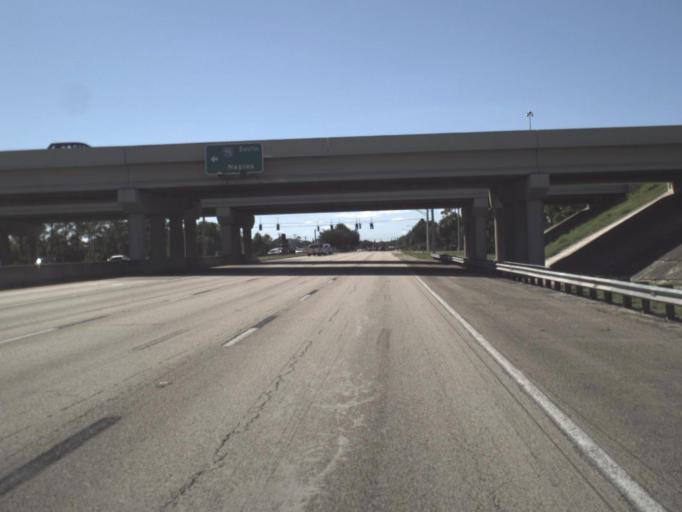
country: US
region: Florida
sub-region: Lee County
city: Gateway
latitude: 26.5475
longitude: -81.7942
